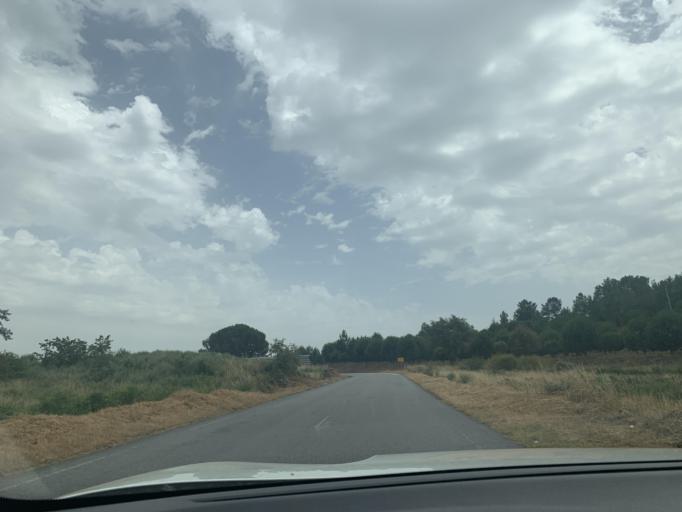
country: PT
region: Viseu
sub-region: Mangualde
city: Mangualde
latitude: 40.5629
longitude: -7.6989
